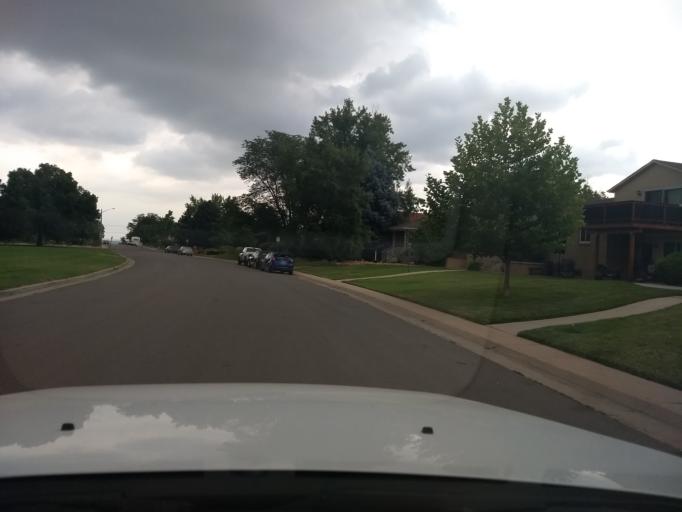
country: US
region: Colorado
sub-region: Denver County
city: Denver
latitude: 39.7013
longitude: -105.0135
